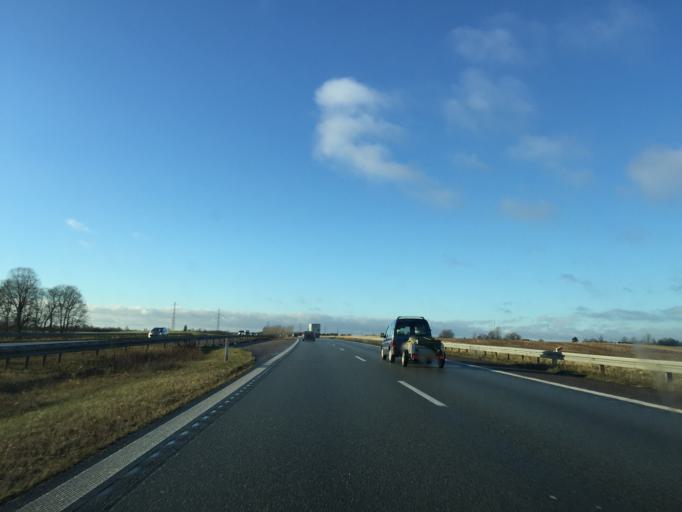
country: DK
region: Zealand
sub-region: Koge Kommune
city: Borup
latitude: 55.4569
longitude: 11.8878
